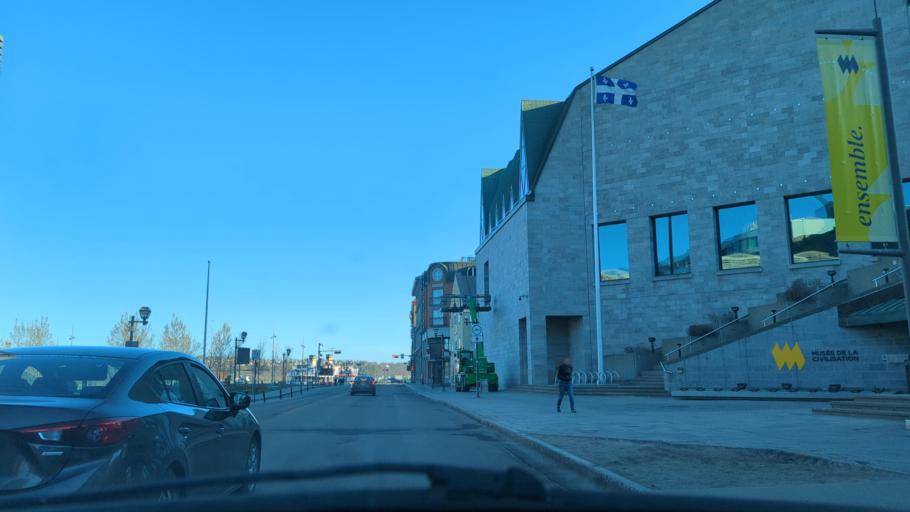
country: CA
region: Quebec
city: Quebec
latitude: 46.8154
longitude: -71.2020
